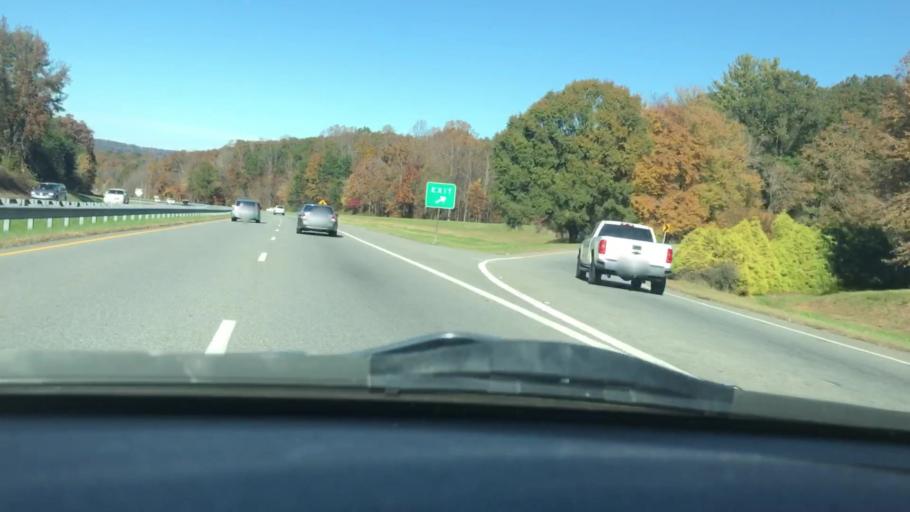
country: US
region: North Carolina
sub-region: Rockingham County
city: Madison
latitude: 36.3753
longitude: -79.9419
